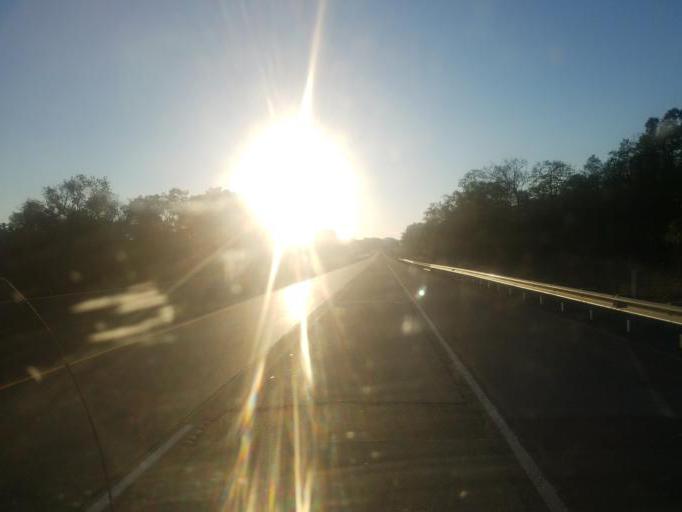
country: US
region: Pennsylvania
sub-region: Butler County
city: Fernway
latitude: 40.7224
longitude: -80.1505
